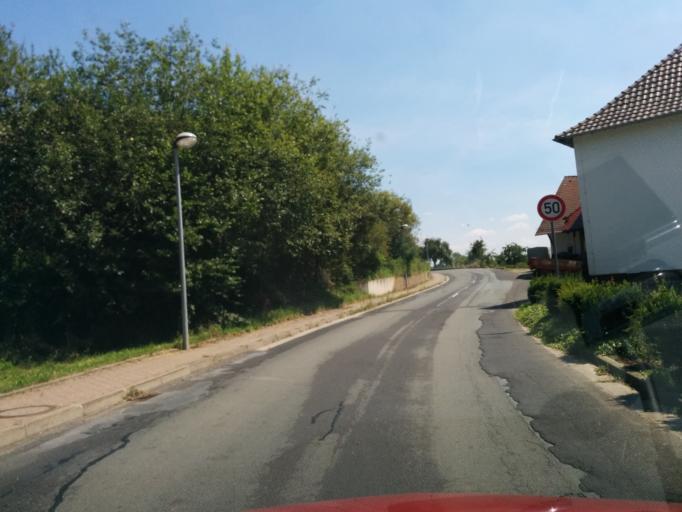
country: DE
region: Hesse
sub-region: Regierungsbezirk Kassel
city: Jesberg
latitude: 51.0154
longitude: 9.1773
